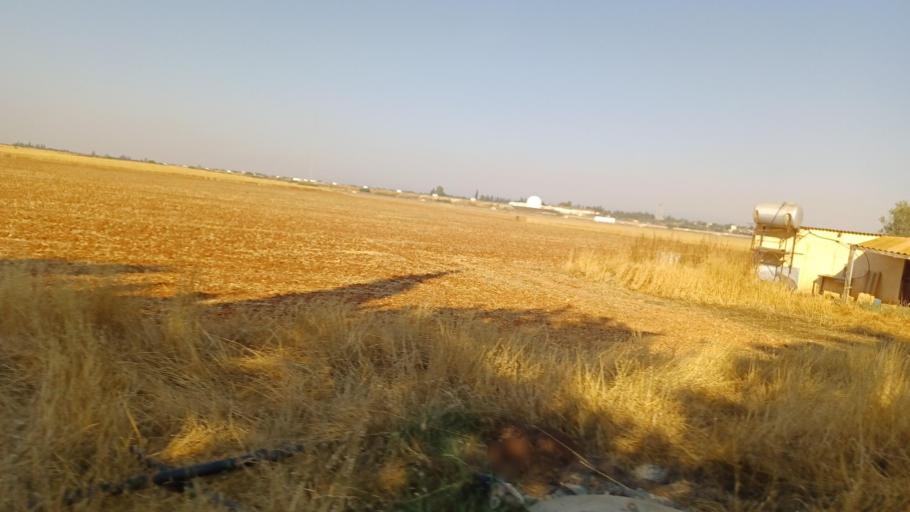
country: CY
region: Ammochostos
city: Famagusta
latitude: 35.0858
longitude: 33.9080
